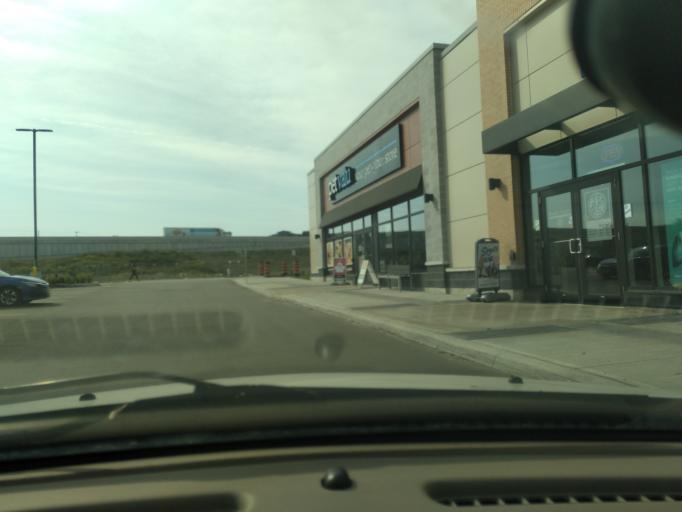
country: CA
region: Ontario
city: Barrie
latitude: 44.4153
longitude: -79.6757
